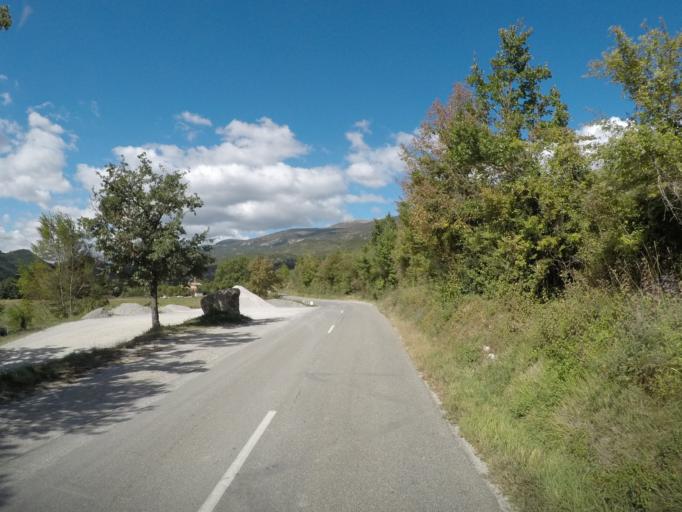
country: FR
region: Provence-Alpes-Cote d'Azur
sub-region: Departement des Hautes-Alpes
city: Laragne-Monteglin
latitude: 44.1684
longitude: 5.7610
